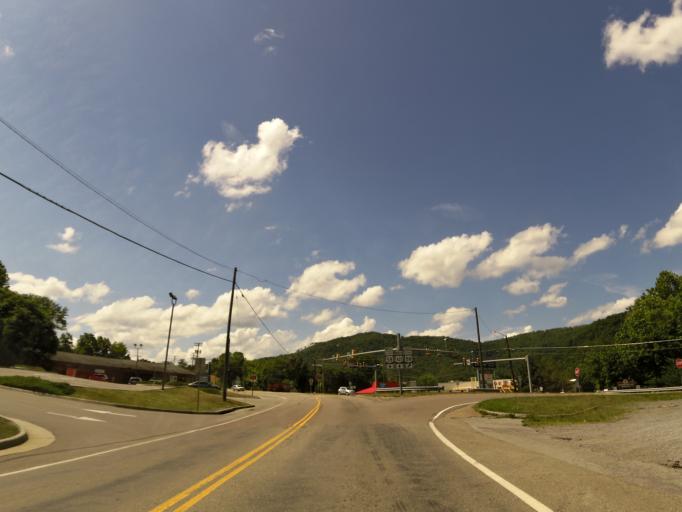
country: US
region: Virginia
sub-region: Lee County
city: Pennington Gap
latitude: 36.7607
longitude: -83.0147
